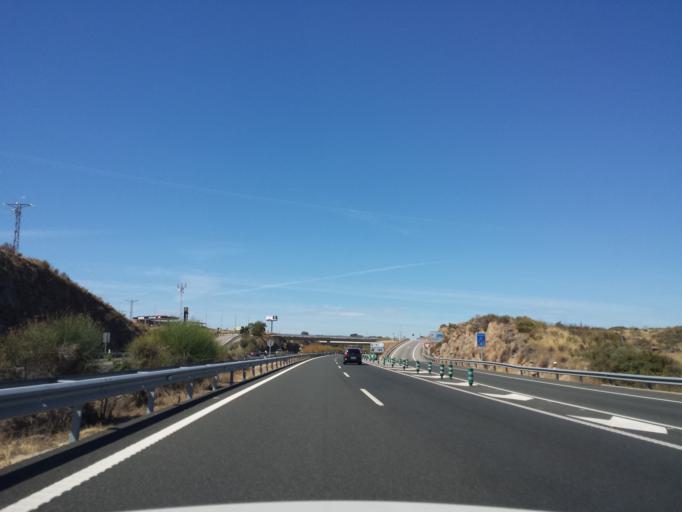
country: ES
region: Extremadura
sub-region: Provincia de Caceres
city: Navalmoral de la Mata
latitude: 39.8757
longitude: -5.5467
